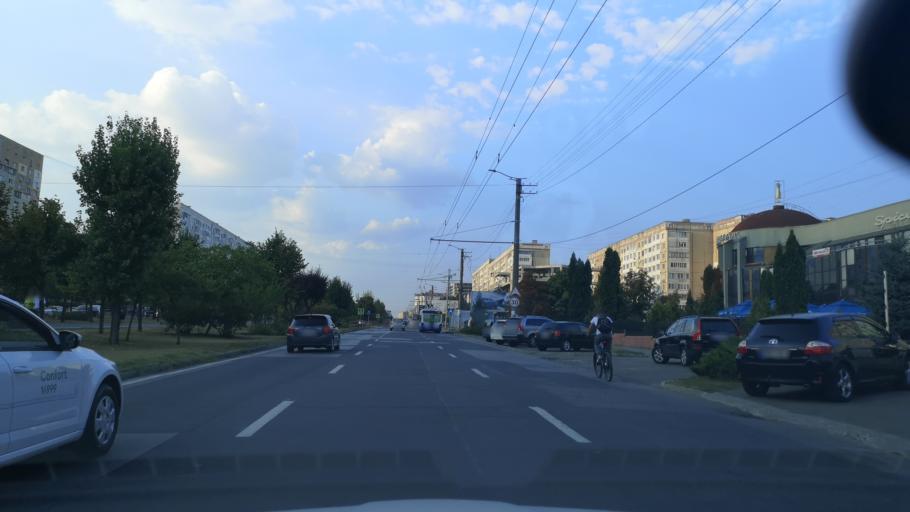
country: MD
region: Chisinau
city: Chisinau
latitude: 47.0390
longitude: 28.8901
